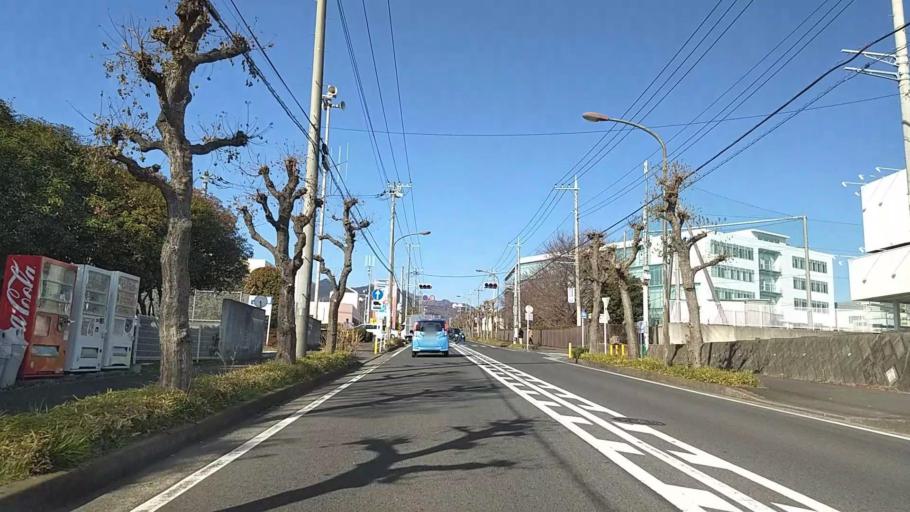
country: JP
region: Kanagawa
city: Isehara
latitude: 35.4016
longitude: 139.2971
